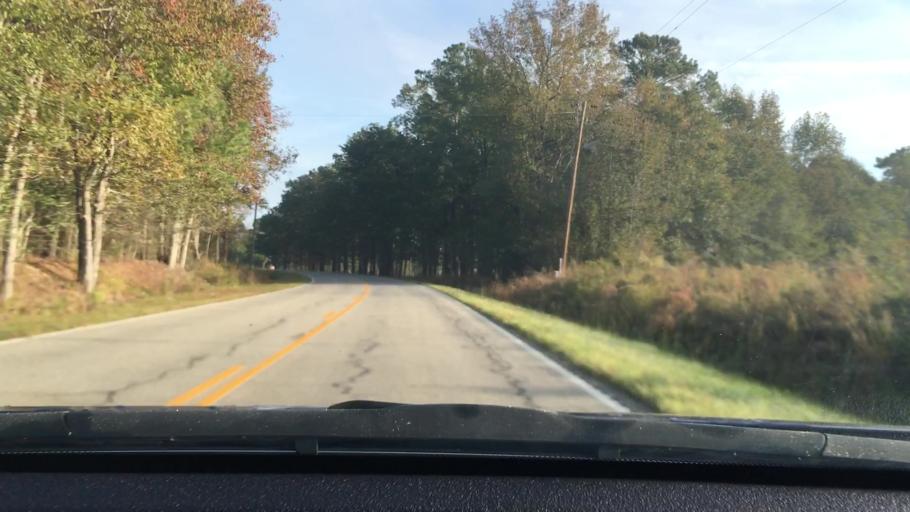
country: US
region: South Carolina
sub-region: Sumter County
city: East Sumter
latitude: 33.9960
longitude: -80.2899
